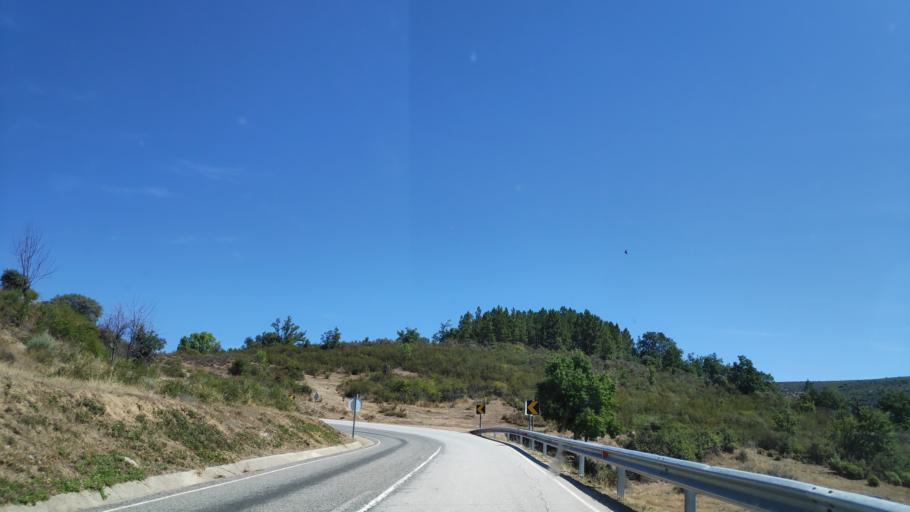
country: PT
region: Braganca
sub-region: Braganca Municipality
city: Braganca
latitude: 41.9001
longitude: -6.7285
